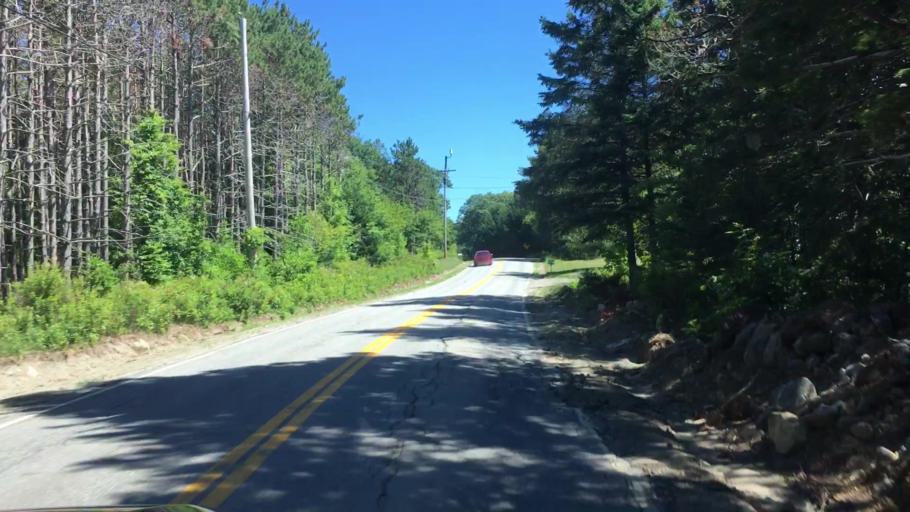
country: US
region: Maine
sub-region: Hancock County
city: Penobscot
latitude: 44.4356
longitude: -68.7131
